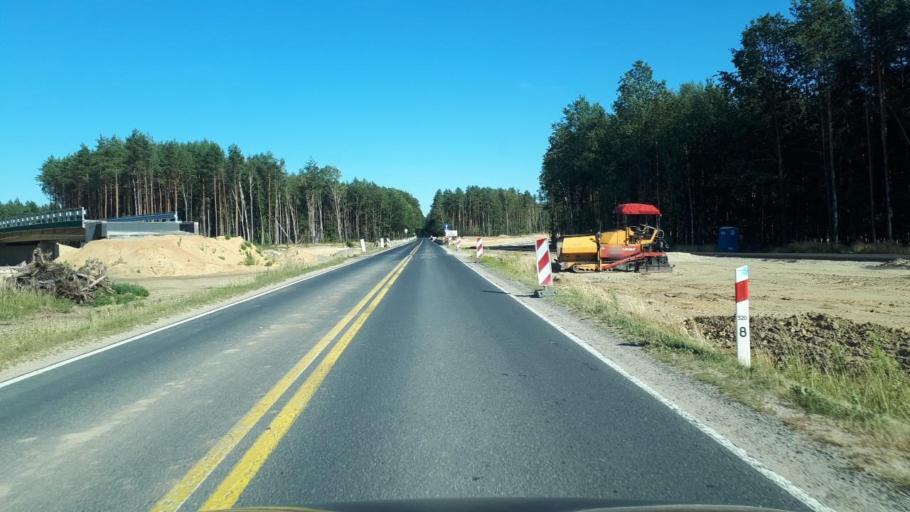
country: PL
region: Silesian Voivodeship
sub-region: Powiat lubliniecki
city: Sierakow Slaski
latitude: 50.8161
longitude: 18.5430
